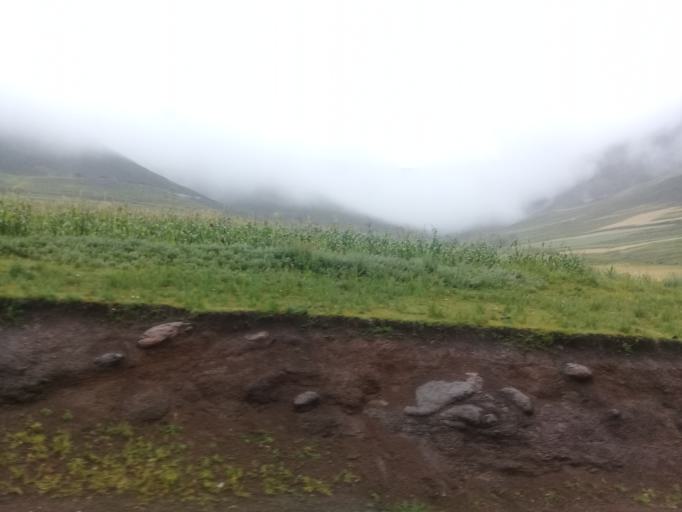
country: LS
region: Mokhotlong
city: Mokhotlong
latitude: -29.3878
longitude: 28.9554
